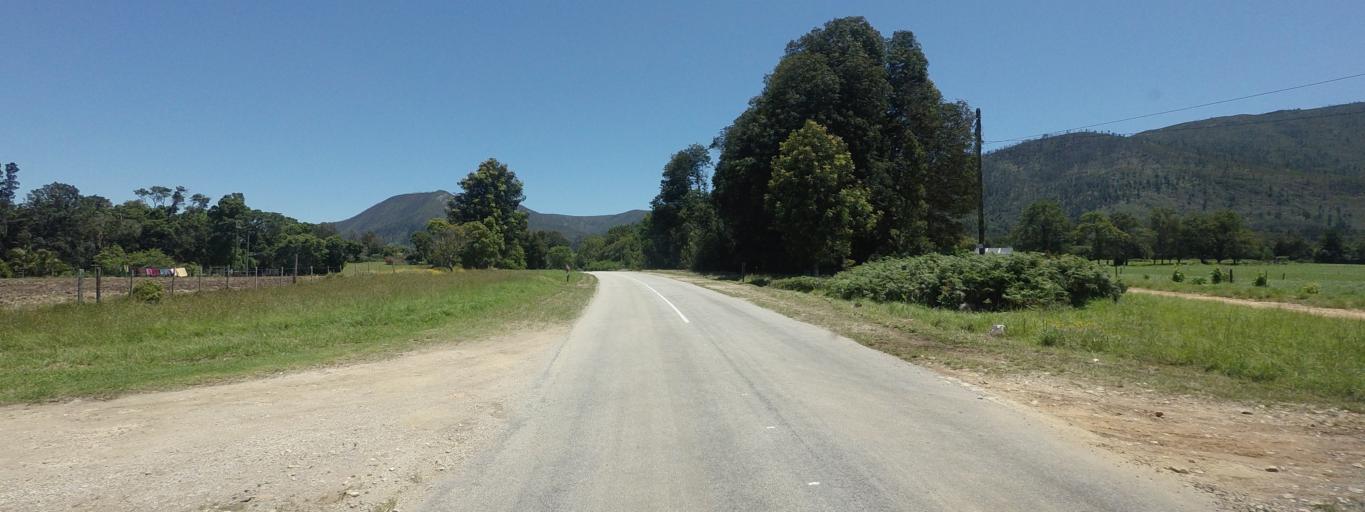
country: ZA
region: Western Cape
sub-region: Eden District Municipality
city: Plettenberg Bay
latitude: -33.9386
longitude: 23.5093
